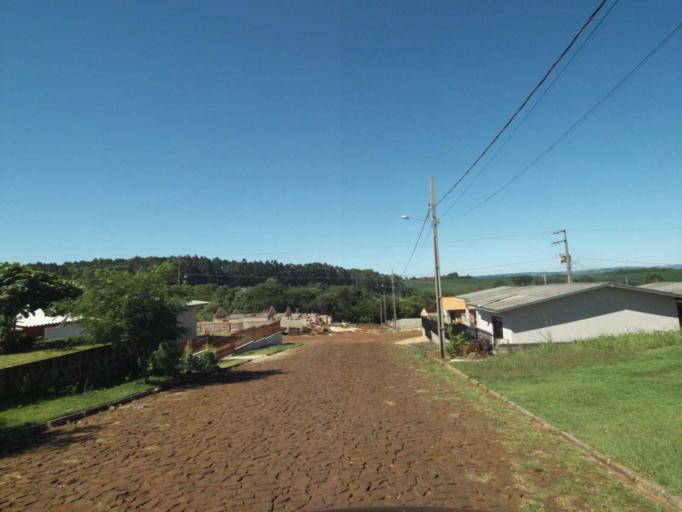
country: BR
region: Parana
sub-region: Coronel Vivida
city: Coronel Vivida
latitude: -25.9597
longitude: -52.8083
